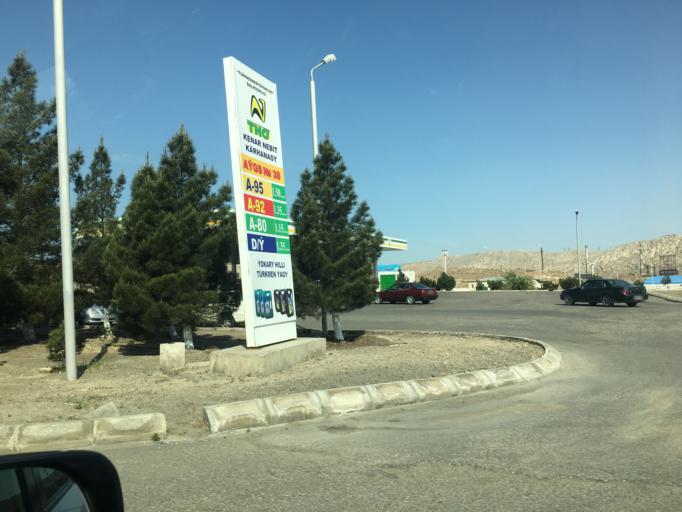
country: TM
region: Balkan
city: Turkmenbasy
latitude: 40.0138
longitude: 52.9515
